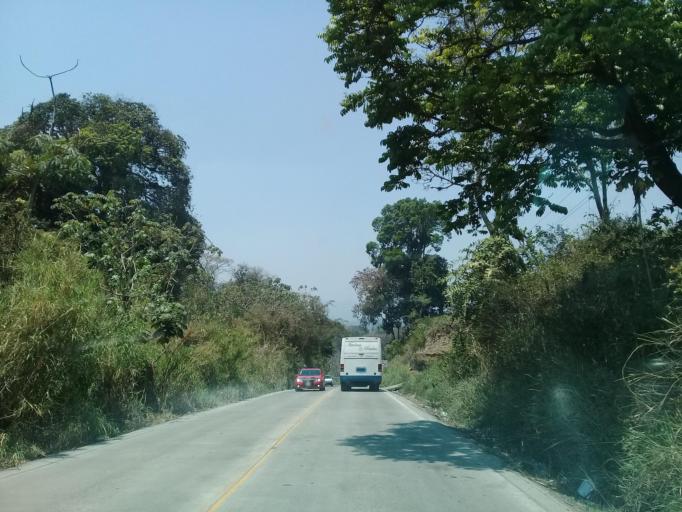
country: MX
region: Veracruz
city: Paraje Nuevo
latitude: 18.8683
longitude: -96.8760
